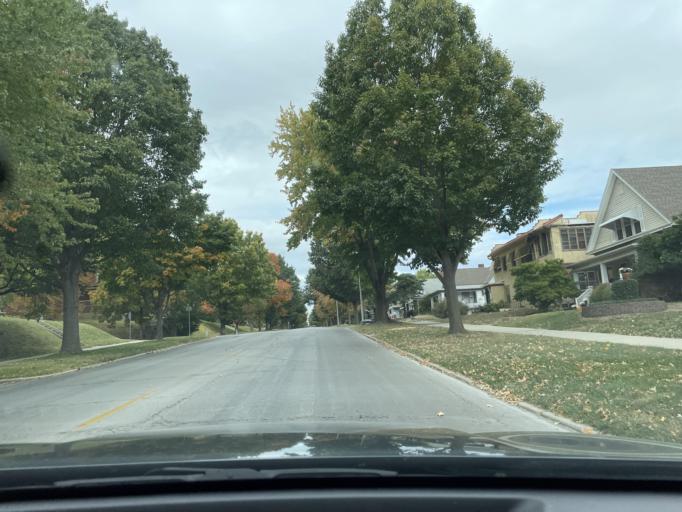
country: US
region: Missouri
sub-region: Buchanan County
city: Saint Joseph
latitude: 39.7697
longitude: -94.8247
